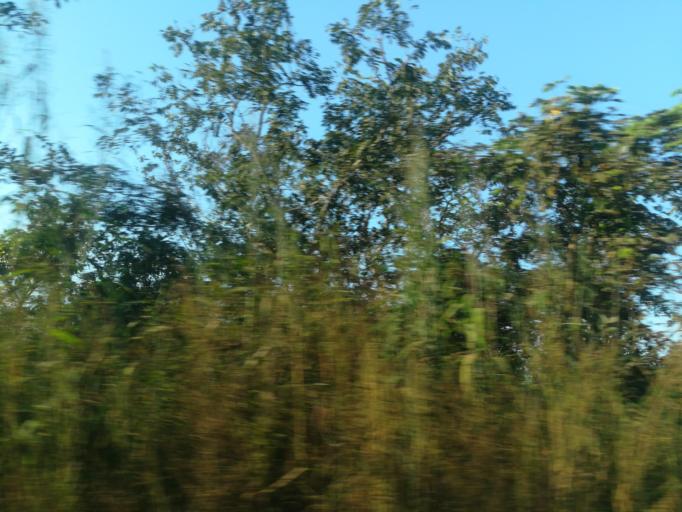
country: NG
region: Ogun
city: Abeokuta
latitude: 7.2132
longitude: 3.1920
